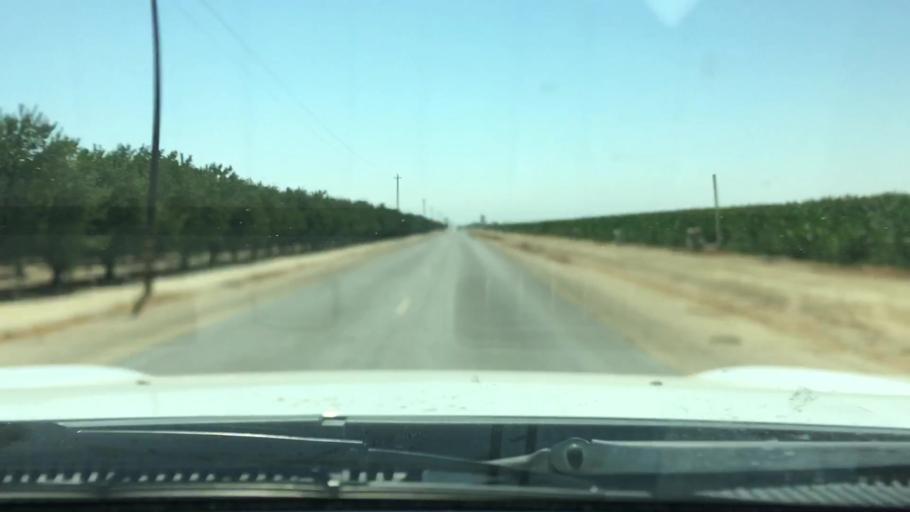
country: US
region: California
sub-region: Kern County
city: Wasco
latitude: 35.5752
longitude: -119.4028
